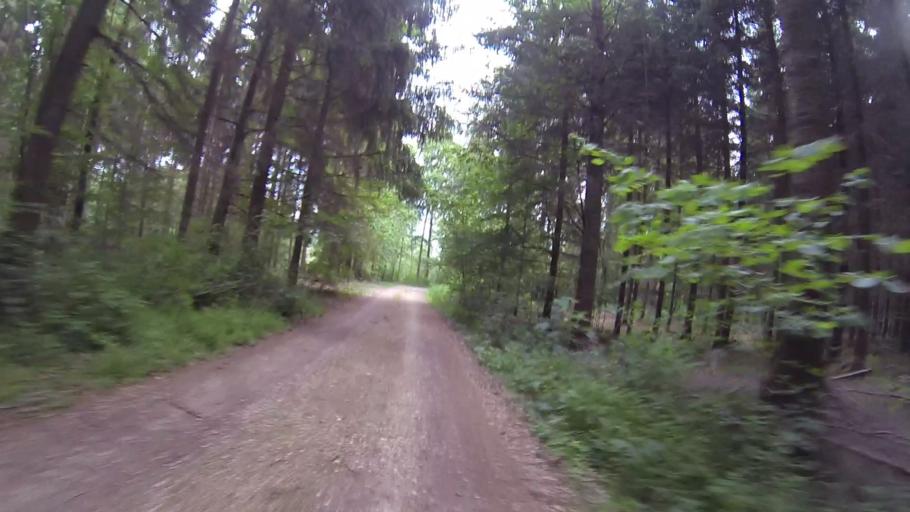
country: DE
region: Baden-Wuerttemberg
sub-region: Tuebingen Region
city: Setzingen
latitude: 48.5575
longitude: 10.1380
